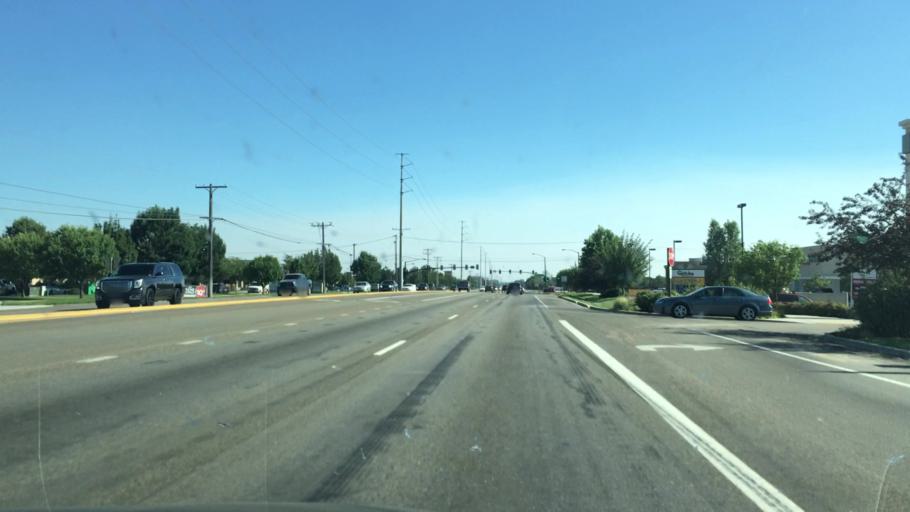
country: US
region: Idaho
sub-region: Ada County
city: Meridian
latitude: 43.6361
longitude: -116.3544
